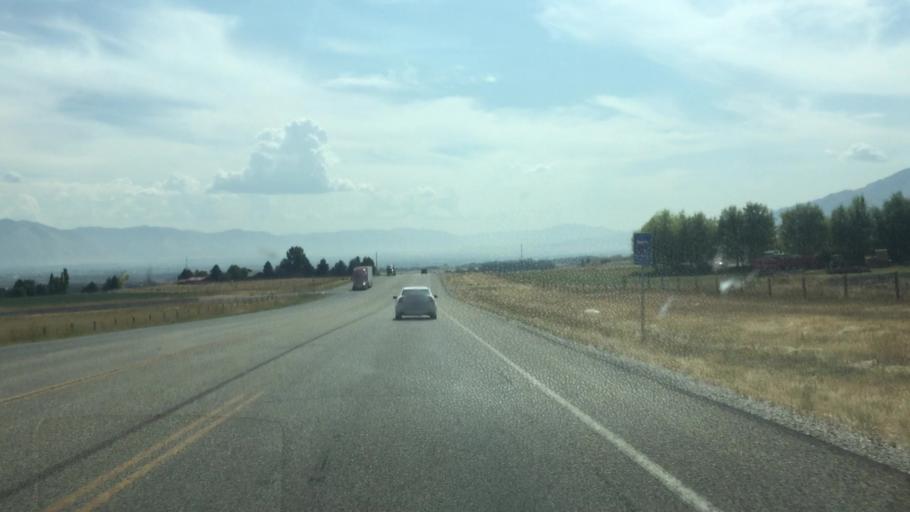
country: US
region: Utah
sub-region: Cache County
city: Mendon
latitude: 41.7646
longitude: -112.0102
